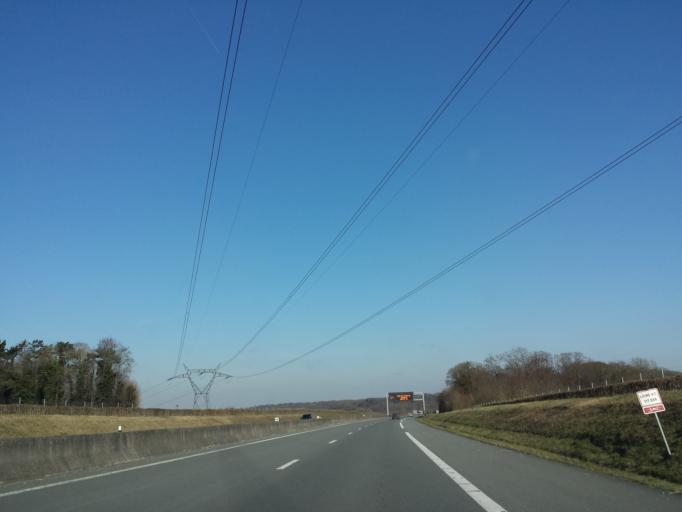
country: FR
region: Picardie
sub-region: Departement de la Somme
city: Saleux
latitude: 49.8207
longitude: 2.2470
